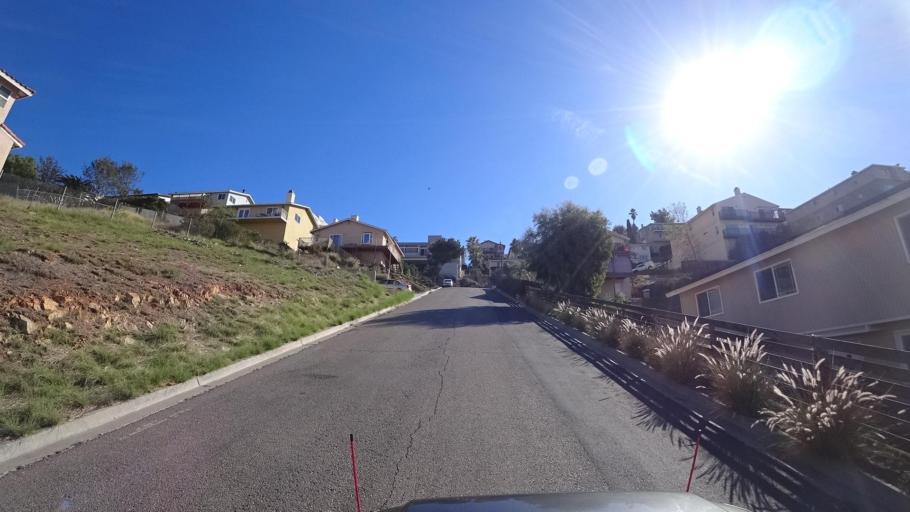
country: US
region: California
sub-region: San Diego County
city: La Presa
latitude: 32.7166
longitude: -116.9881
